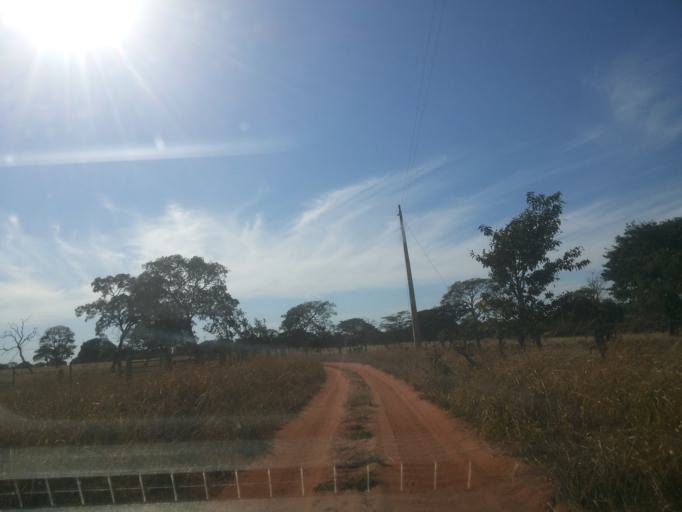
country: BR
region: Minas Gerais
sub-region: Ituiutaba
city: Ituiutaba
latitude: -19.1239
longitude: -49.3885
